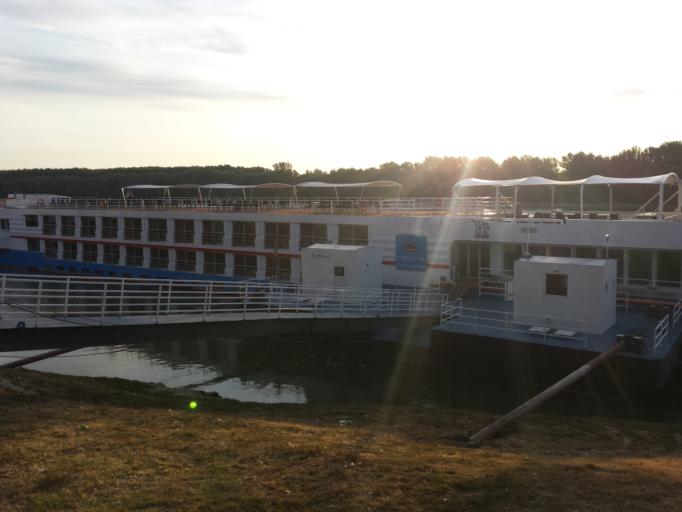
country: RO
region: Braila
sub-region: Municipiul Braila
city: Braila
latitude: 45.2695
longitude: 27.9809
